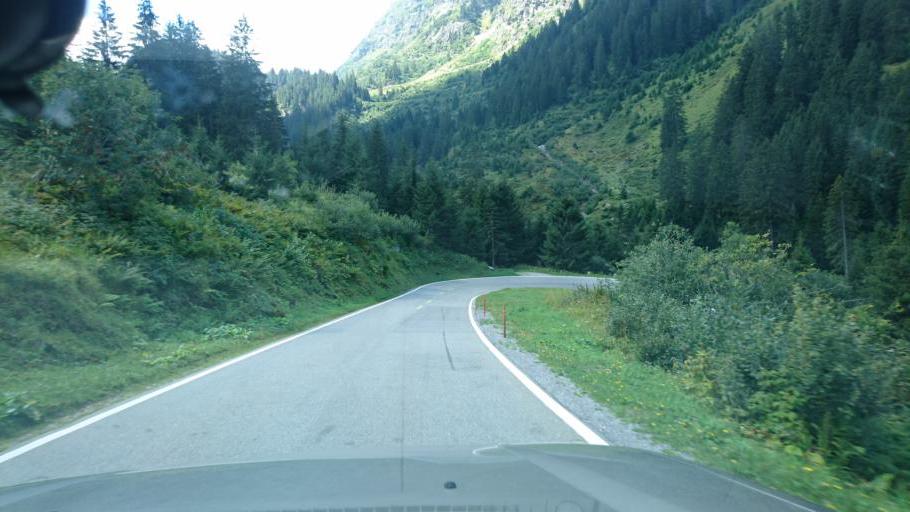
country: AT
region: Vorarlberg
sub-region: Politischer Bezirk Bludenz
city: Gaschurn
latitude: 46.9489
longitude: 10.0695
